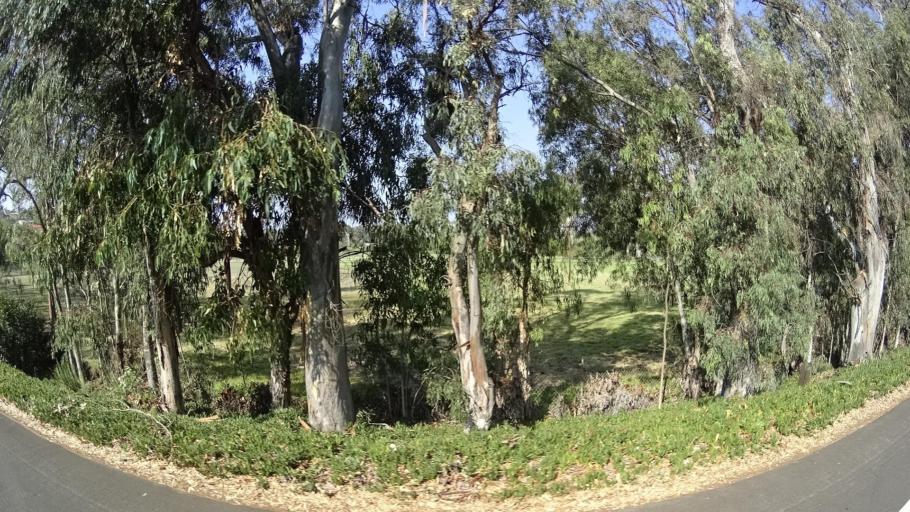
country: US
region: California
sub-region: San Diego County
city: Vista
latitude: 33.2323
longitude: -117.2496
